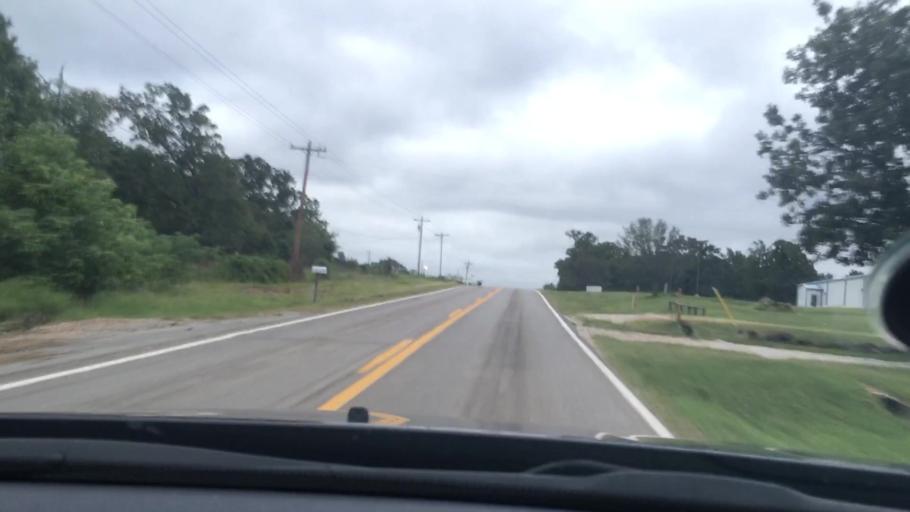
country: US
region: Oklahoma
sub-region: Sequoyah County
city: Vian
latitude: 35.6025
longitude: -95.0138
